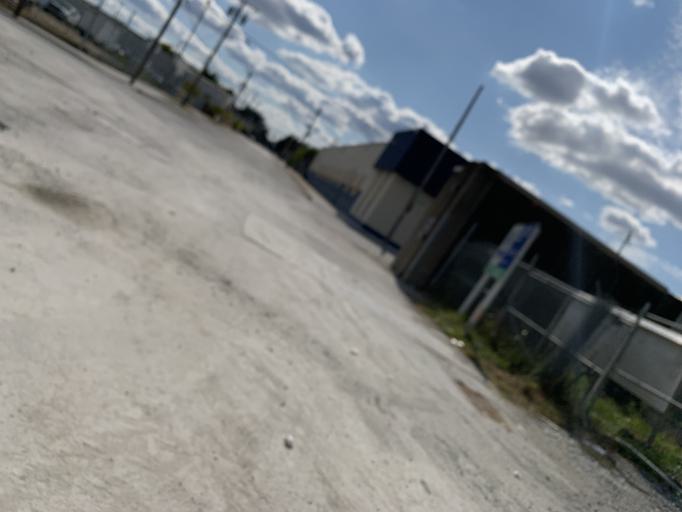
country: US
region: Kentucky
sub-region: Jefferson County
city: Louisville
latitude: 38.2596
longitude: -85.7695
